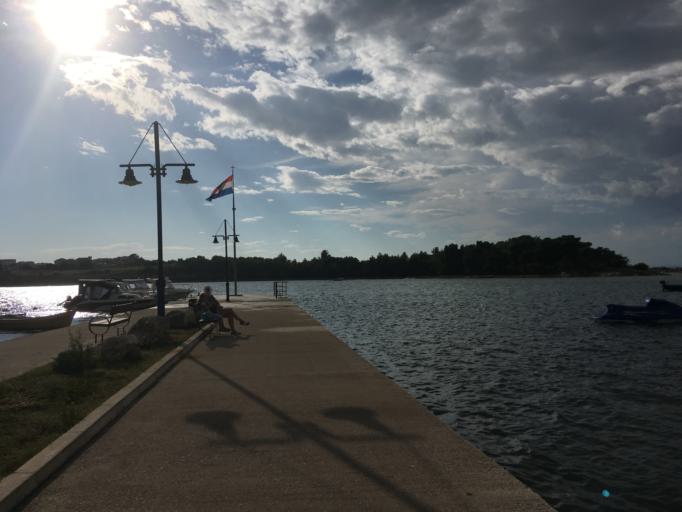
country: HR
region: Zadarska
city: Nin
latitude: 44.2437
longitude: 15.1816
